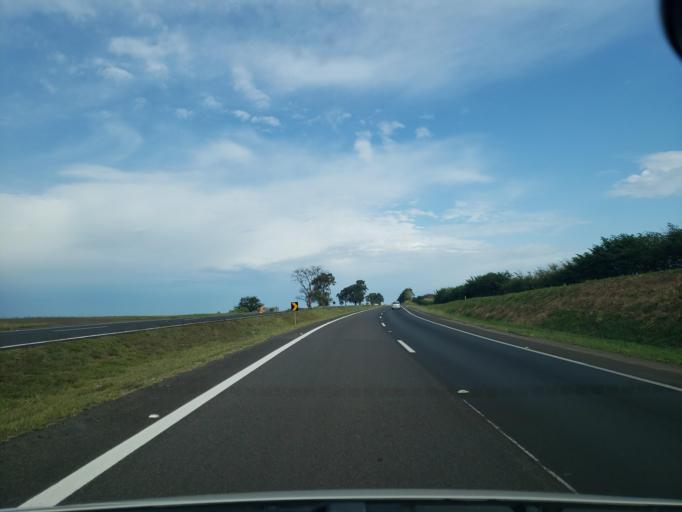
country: BR
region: Sao Paulo
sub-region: Brotas
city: Brotas
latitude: -22.2836
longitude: -47.9915
